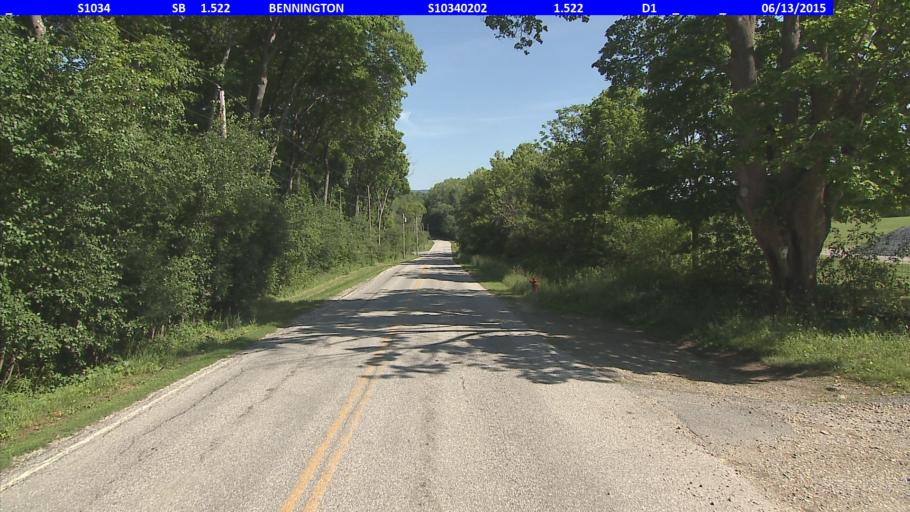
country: US
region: Vermont
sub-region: Bennington County
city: Bennington
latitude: 42.8724
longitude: -73.2123
